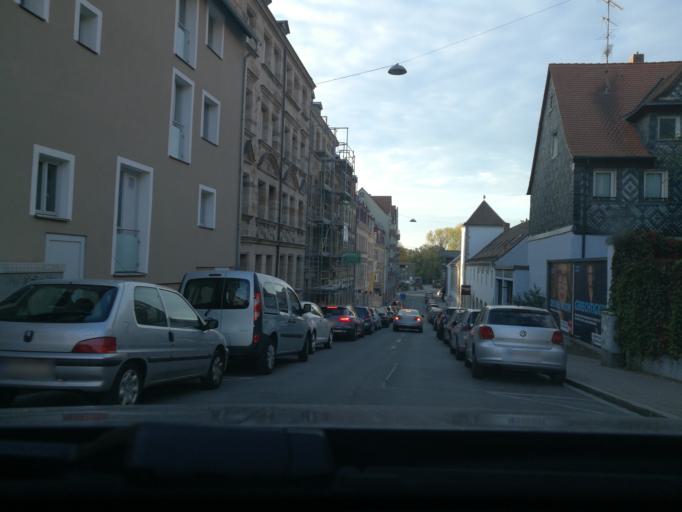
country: DE
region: Bavaria
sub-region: Regierungsbezirk Mittelfranken
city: Furth
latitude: 49.4800
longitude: 10.9873
